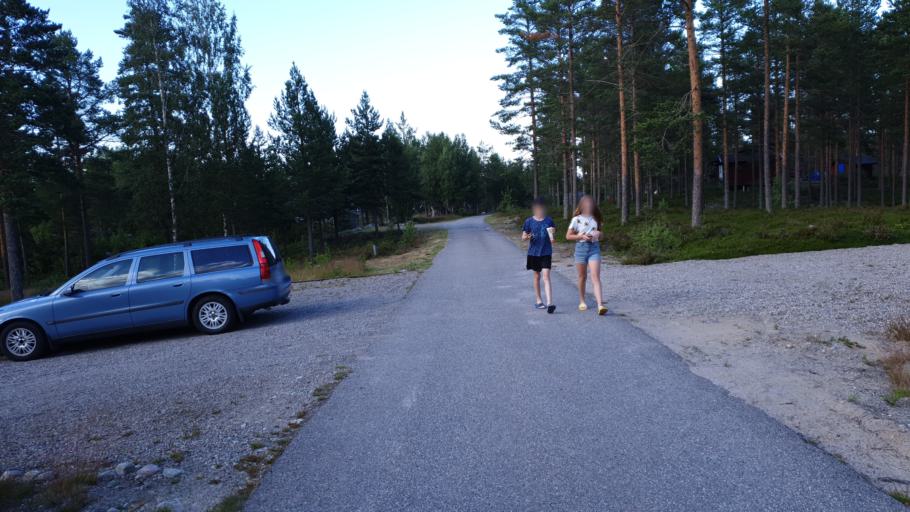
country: SE
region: Gaevleborg
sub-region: Soderhamns Kommun
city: Marielund
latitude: 61.4249
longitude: 17.1546
